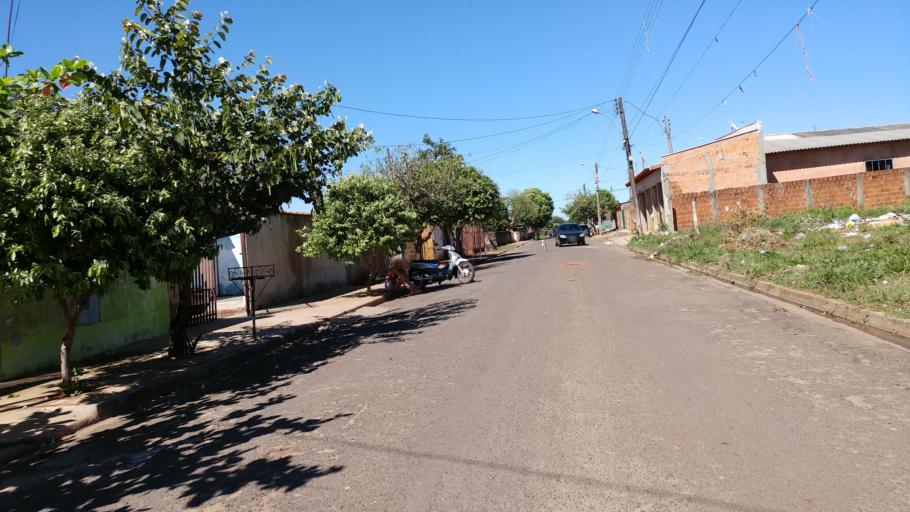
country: BR
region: Sao Paulo
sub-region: Paraguacu Paulista
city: Paraguacu Paulista
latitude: -22.4096
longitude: -50.5660
